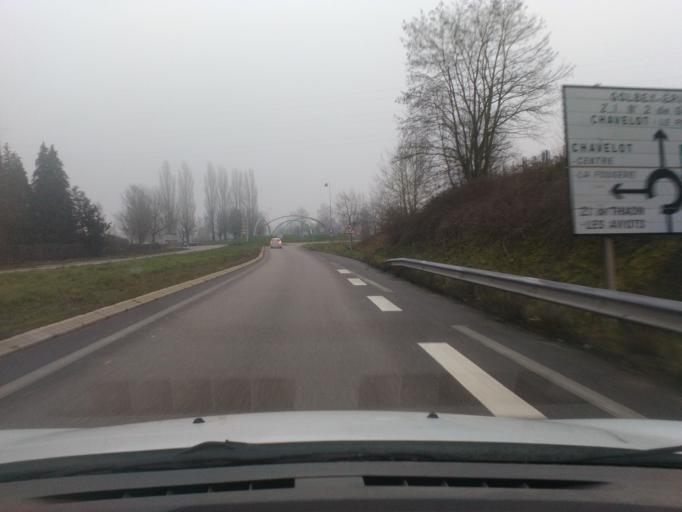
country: FR
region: Lorraine
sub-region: Departement des Vosges
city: Chavelot
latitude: 48.2230
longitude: 6.4336
